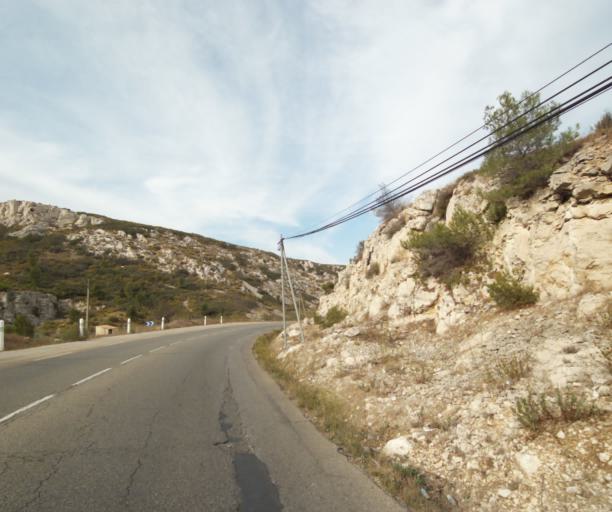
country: FR
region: Provence-Alpes-Cote d'Azur
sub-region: Departement des Bouches-du-Rhone
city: Le Rove
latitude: 43.3665
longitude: 5.2352
